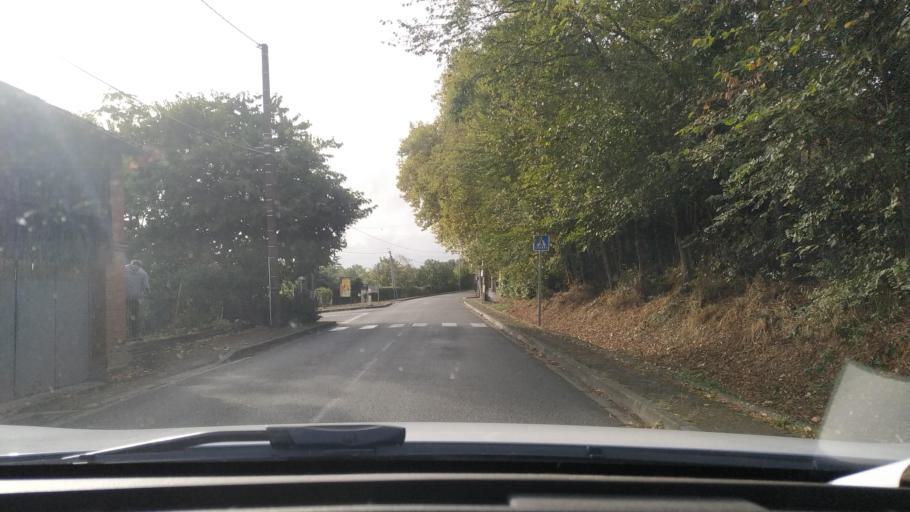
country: FR
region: Midi-Pyrenees
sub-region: Departement de la Haute-Garonne
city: Gaillac-Toulza
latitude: 43.3009
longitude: 1.4694
